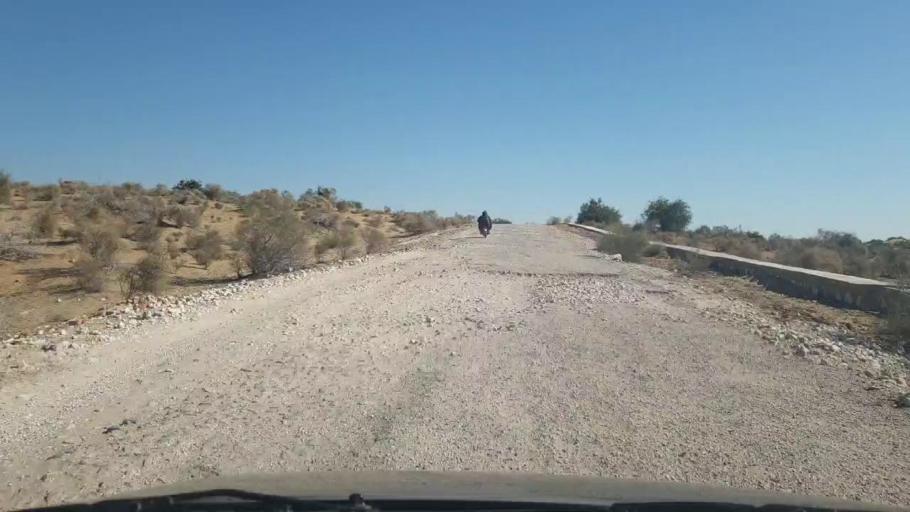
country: PK
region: Sindh
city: Bozdar
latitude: 27.0035
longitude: 68.8829
